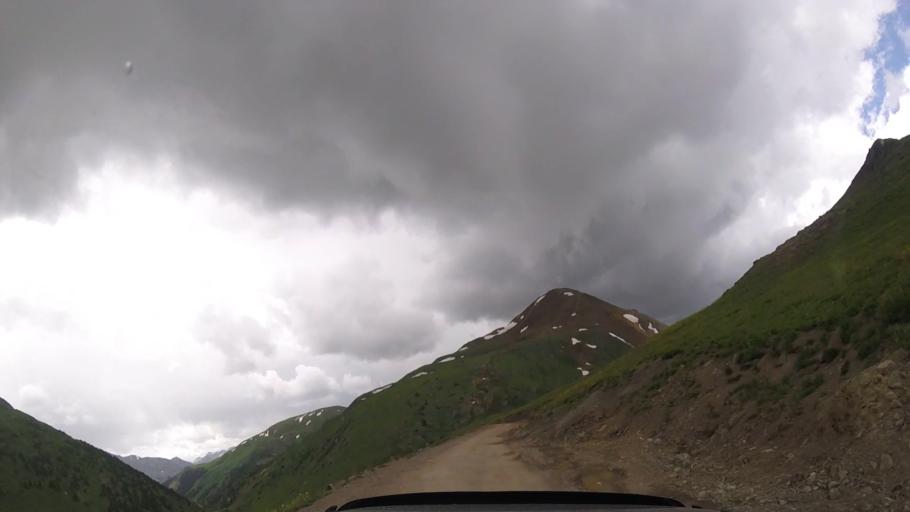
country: US
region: Colorado
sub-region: Ouray County
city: Ouray
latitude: 37.9501
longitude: -107.5754
